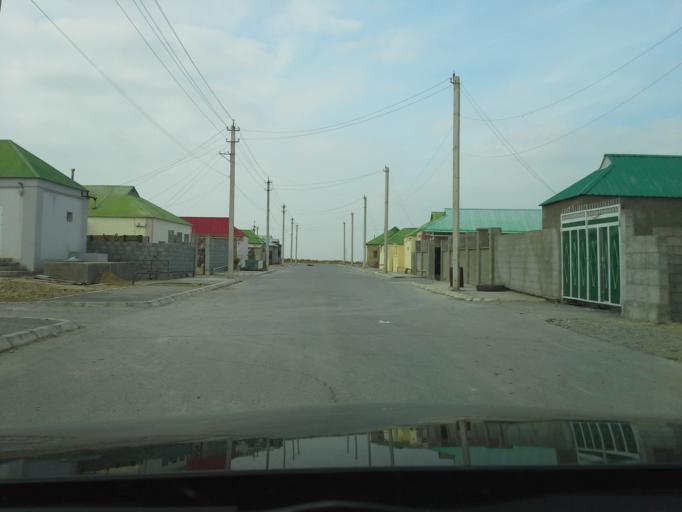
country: TM
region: Ahal
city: Abadan
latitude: 38.0343
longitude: 58.2672
